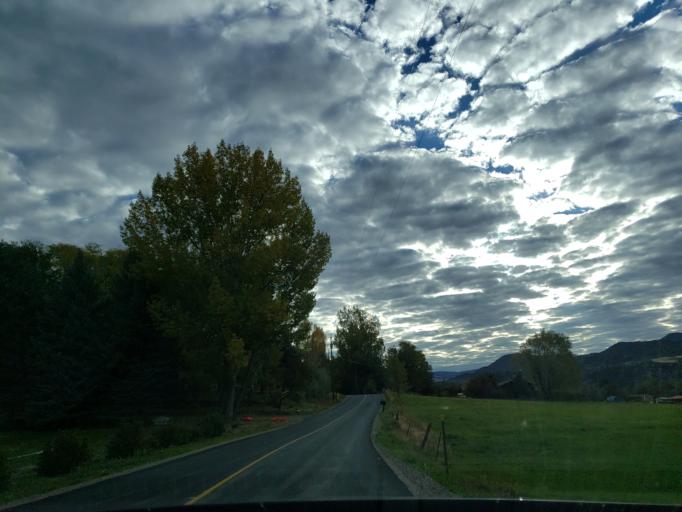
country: US
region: Colorado
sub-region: Garfield County
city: New Castle
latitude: 39.5605
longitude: -107.5648
